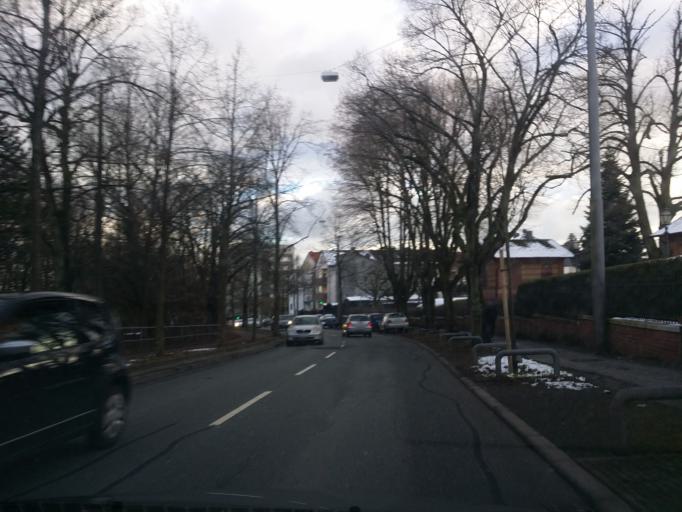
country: DE
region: Hesse
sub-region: Regierungsbezirk Darmstadt
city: Wiesbaden
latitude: 50.0948
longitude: 8.2217
